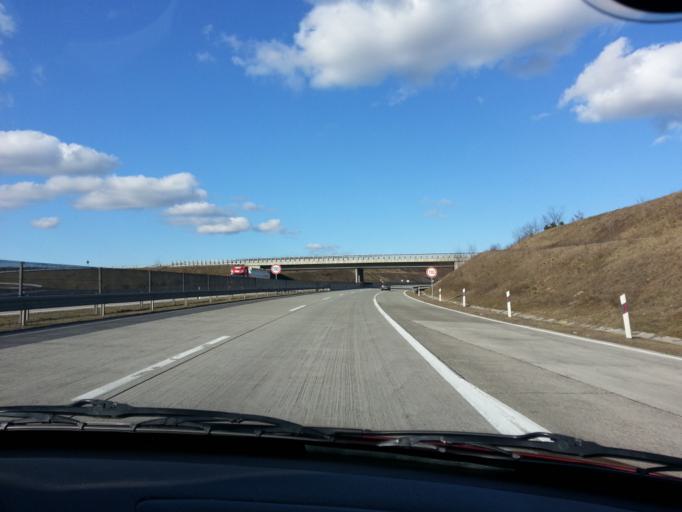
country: HU
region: Pest
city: Kerepes
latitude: 47.5830
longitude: 19.3138
